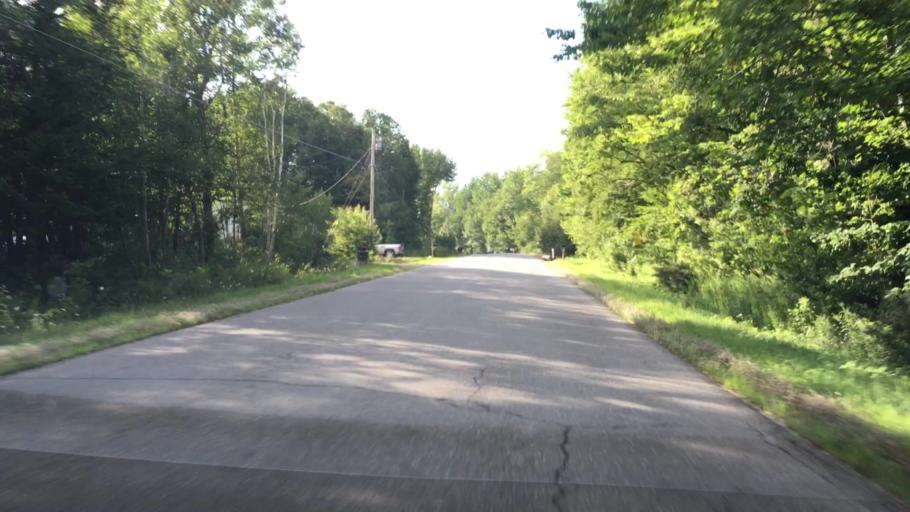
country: US
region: Maine
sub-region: Waldo County
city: Stockton Springs
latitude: 44.4913
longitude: -68.8680
